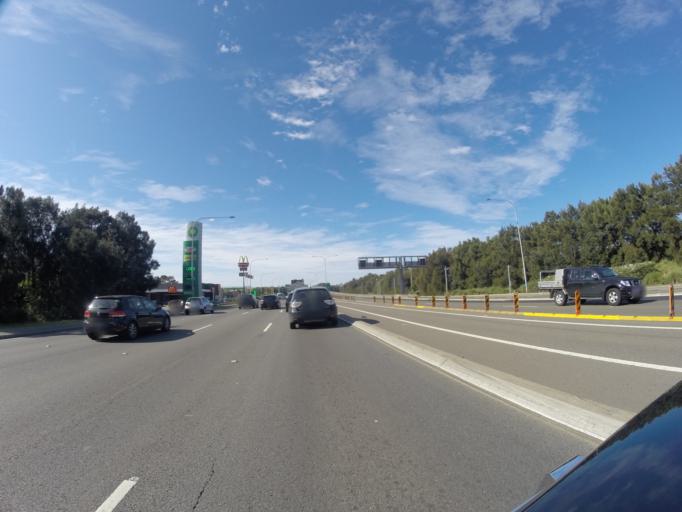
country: AU
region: New South Wales
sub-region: Botany Bay
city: Botany
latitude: -33.9454
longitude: 151.1840
